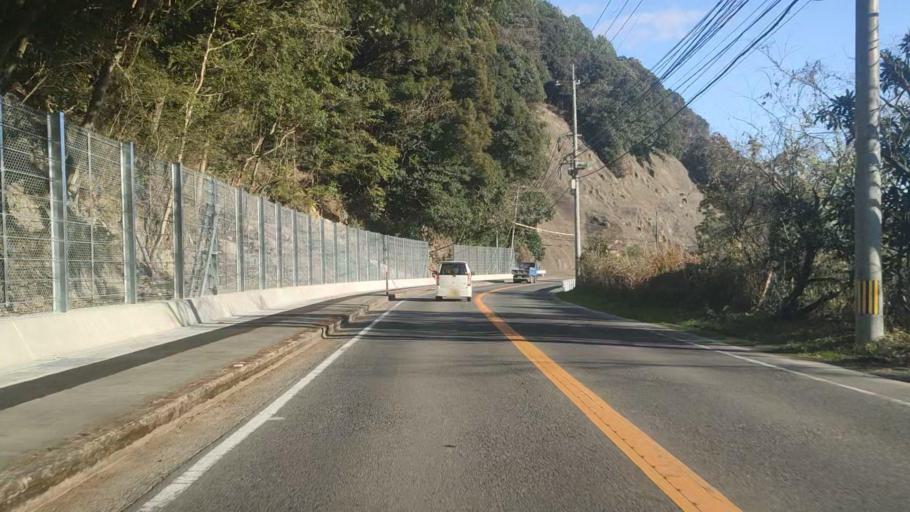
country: JP
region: Saga Prefecture
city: Saga-shi
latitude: 33.3426
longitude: 130.2548
